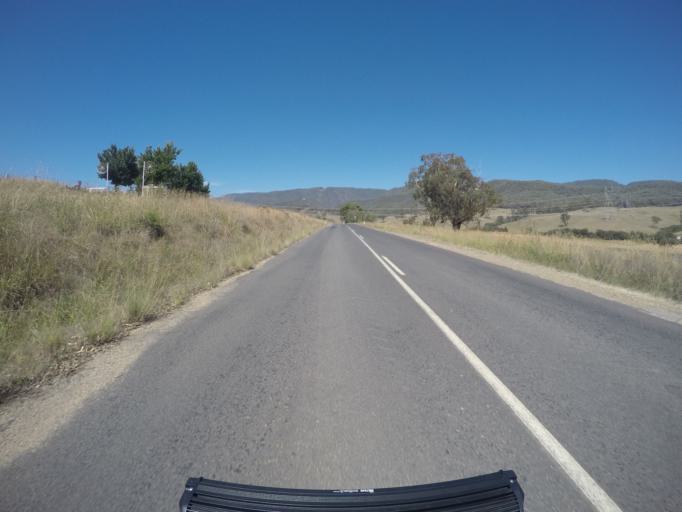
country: AU
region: New South Wales
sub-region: Tumut Shire
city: Tumut
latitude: -35.5974
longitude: 148.2820
